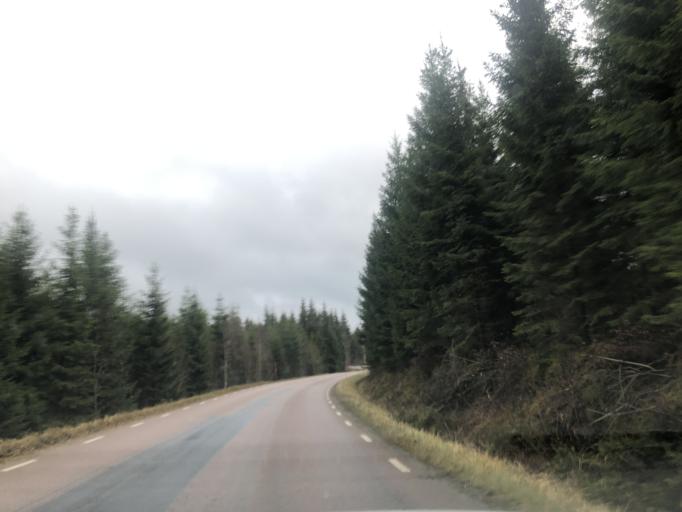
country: SE
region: Vaestra Goetaland
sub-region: Ulricehamns Kommun
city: Ulricehamn
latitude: 57.8324
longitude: 13.4822
